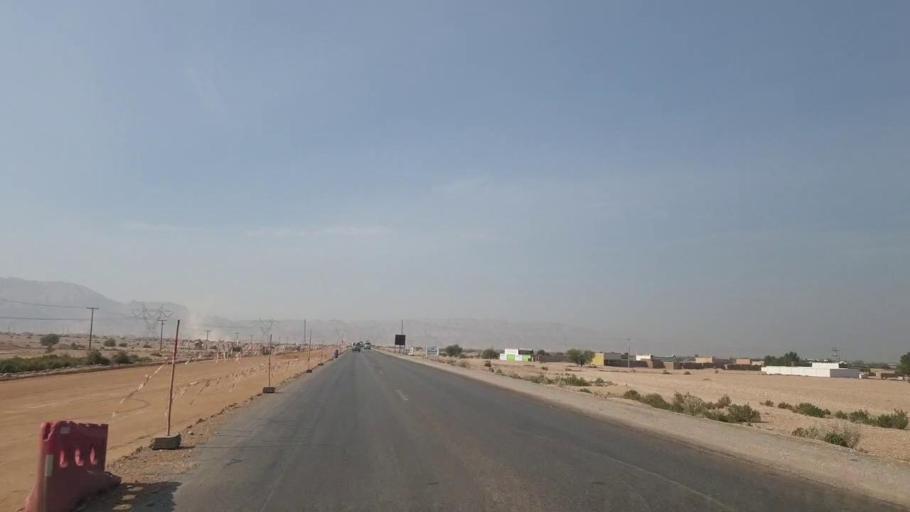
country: PK
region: Sindh
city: Sehwan
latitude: 26.2032
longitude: 67.9345
